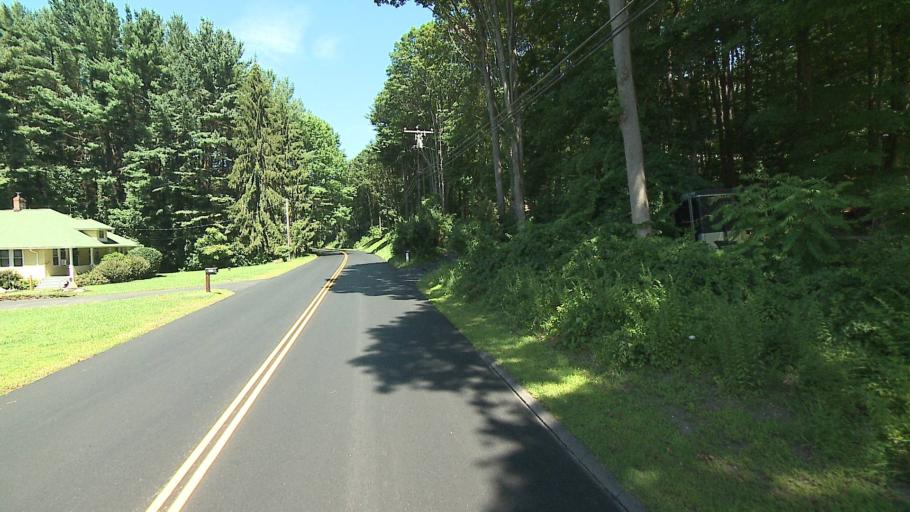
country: US
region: Connecticut
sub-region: Hartford County
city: West Simsbury
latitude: 41.9037
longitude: -72.8940
